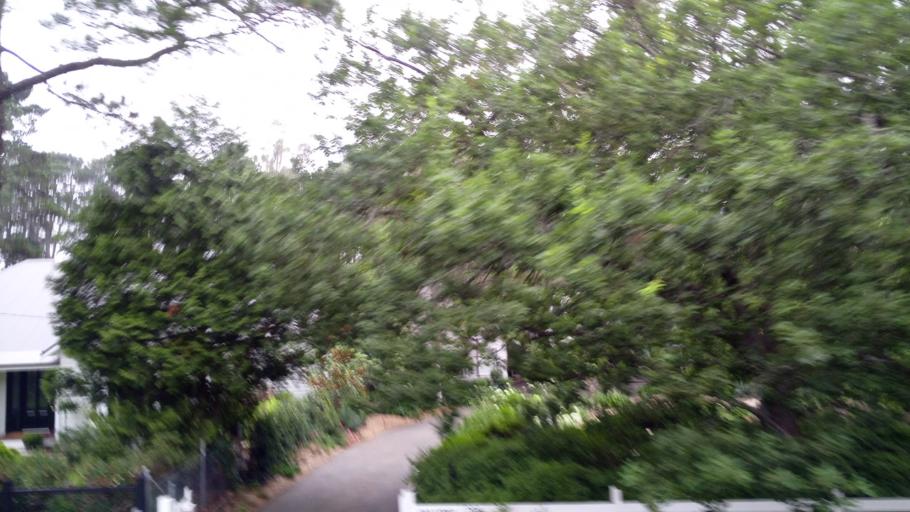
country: AU
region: New South Wales
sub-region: Blue Mountains Municipality
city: Leura
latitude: -33.7217
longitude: 150.3287
